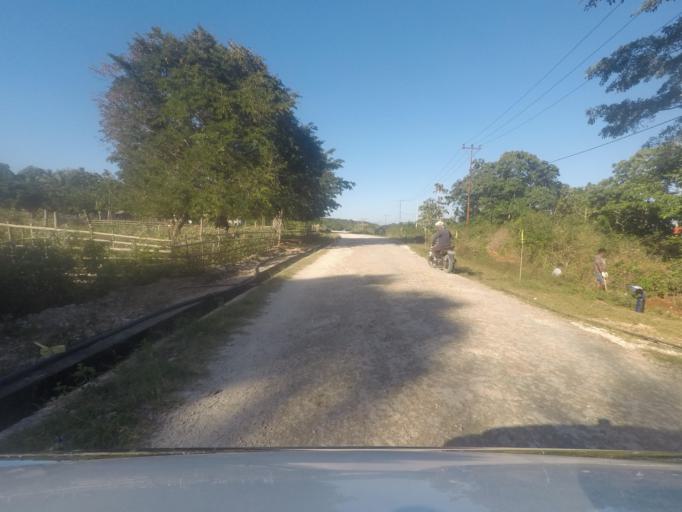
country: TL
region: Lautem
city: Lospalos
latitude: -8.3998
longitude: 127.1945
